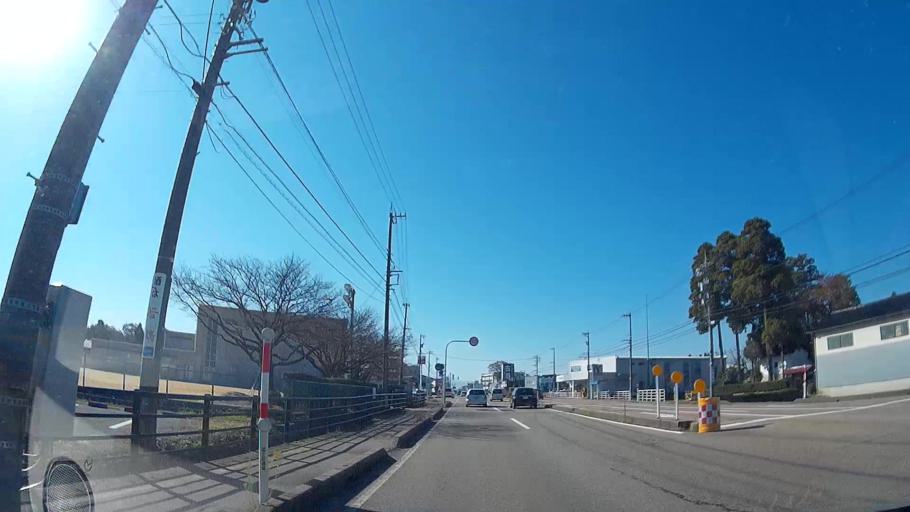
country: JP
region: Toyama
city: Nanto-shi
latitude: 36.6566
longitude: 136.9684
